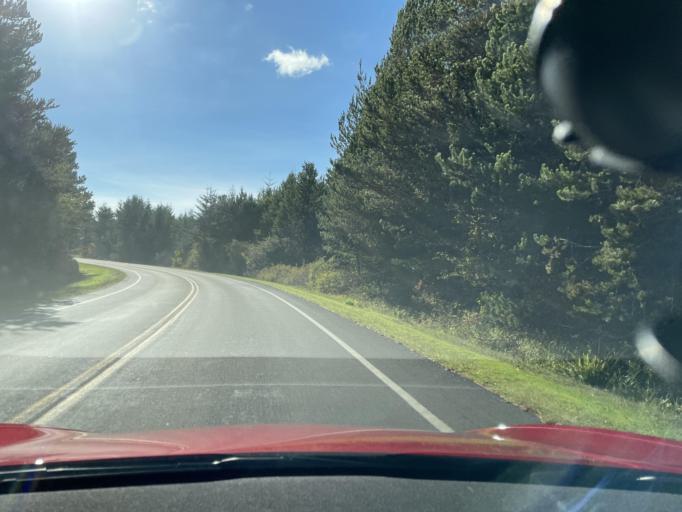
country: US
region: Washington
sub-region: San Juan County
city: Friday Harbor
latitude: 48.4672
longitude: -123.0258
